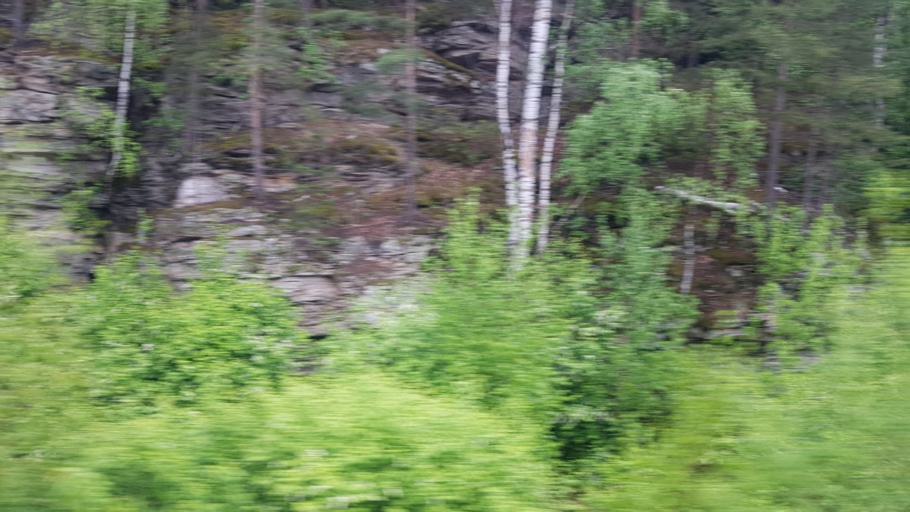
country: NO
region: Oppland
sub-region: Sor-Fron
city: Hundorp
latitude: 61.5670
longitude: 9.9162
